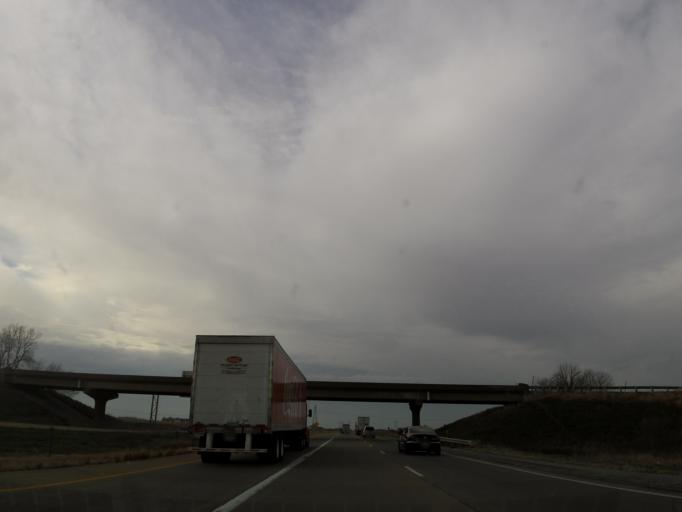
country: US
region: Iowa
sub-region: Scott County
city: Walcott
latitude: 41.6040
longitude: -90.6847
